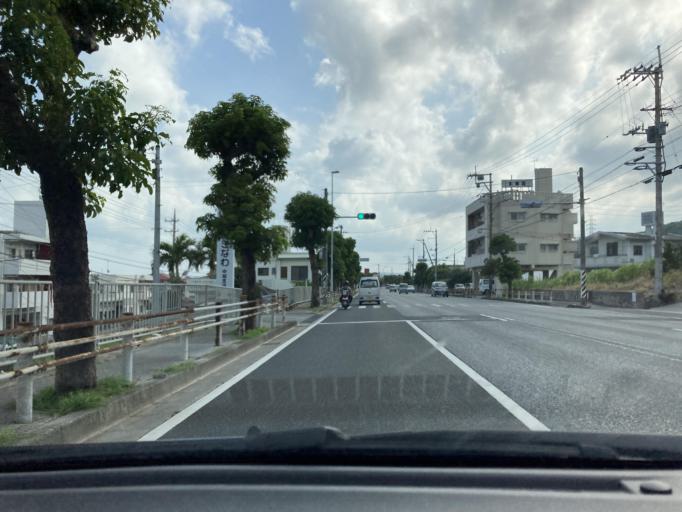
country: JP
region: Okinawa
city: Ginowan
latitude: 26.2666
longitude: 127.7904
